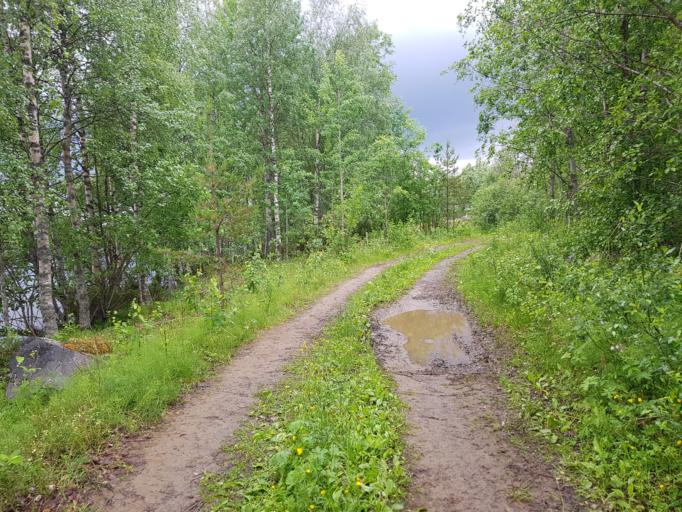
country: RU
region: Republic of Karelia
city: Kostomuksha
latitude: 64.8268
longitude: 29.8843
